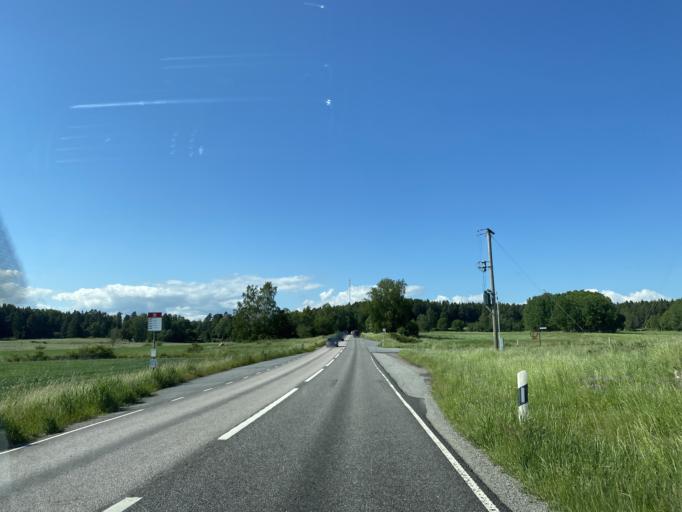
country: SE
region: Stockholm
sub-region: Norrtalje Kommun
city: Norrtalje
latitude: 59.7971
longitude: 18.6581
